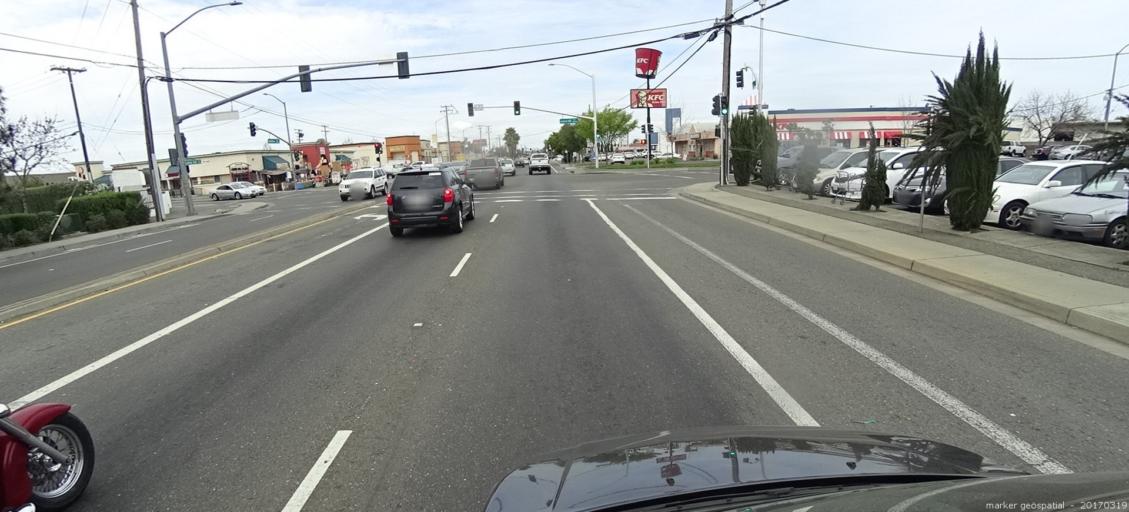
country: US
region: California
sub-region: Sacramento County
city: Parkway
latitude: 38.5154
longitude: -121.4381
